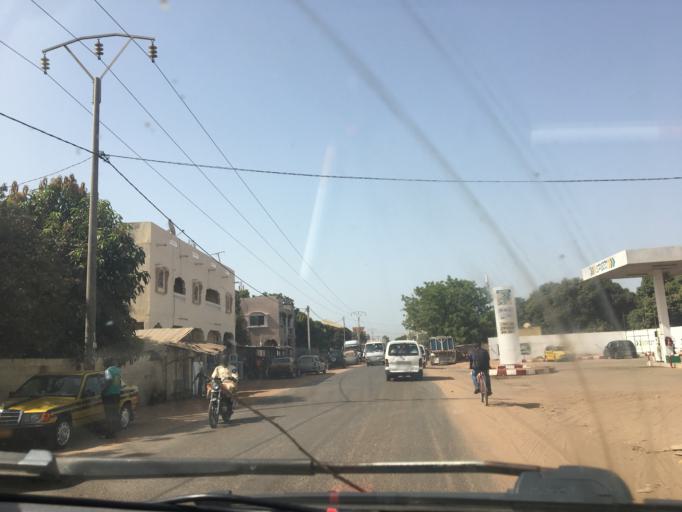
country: GM
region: Western
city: Abuko
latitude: 13.3921
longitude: -16.6747
